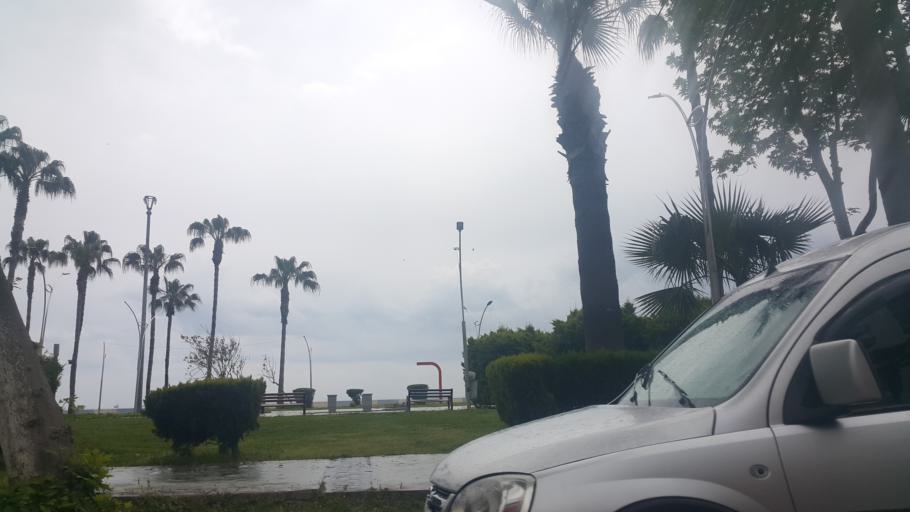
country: TR
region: Mersin
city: Mercin
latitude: 36.7821
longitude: 34.6099
